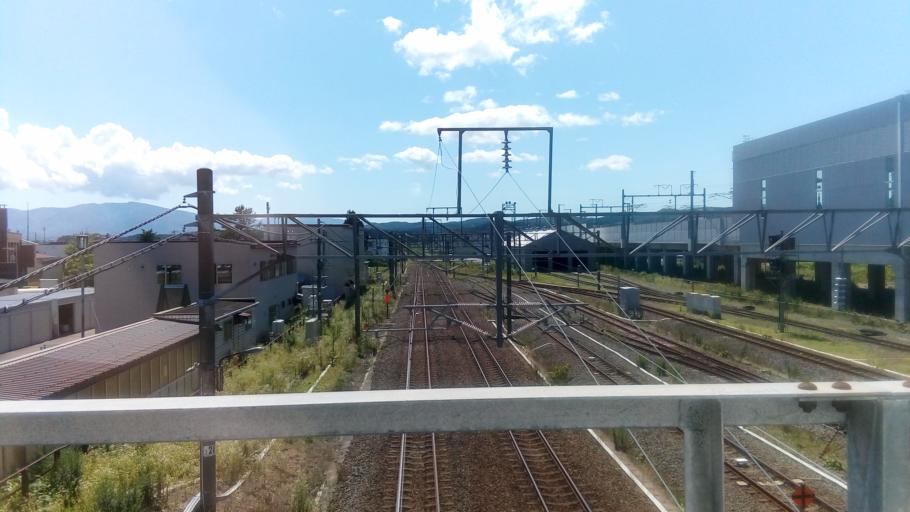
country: JP
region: Hokkaido
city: Kamiiso
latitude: 41.6780
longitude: 140.4344
